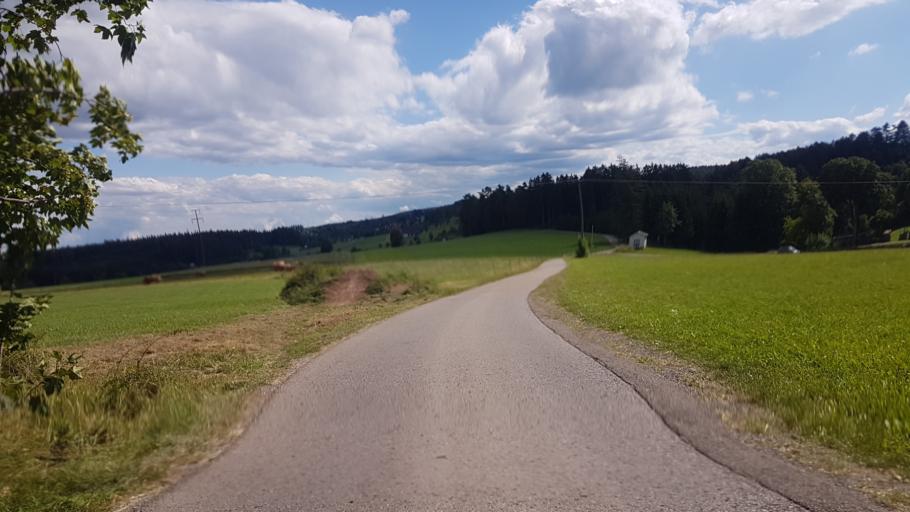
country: DE
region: Baden-Wuerttemberg
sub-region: Freiburg Region
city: Hardt
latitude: 48.1681
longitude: 8.4071
